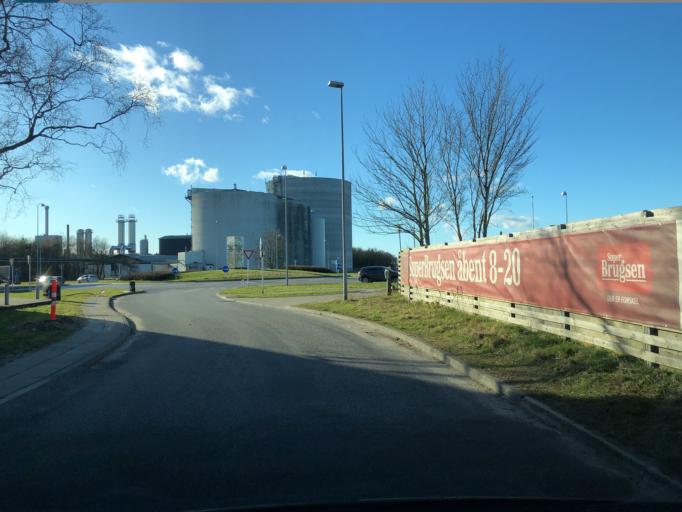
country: DK
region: Central Jutland
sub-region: Viborg Kommune
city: Karup
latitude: 56.3074
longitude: 9.1618
